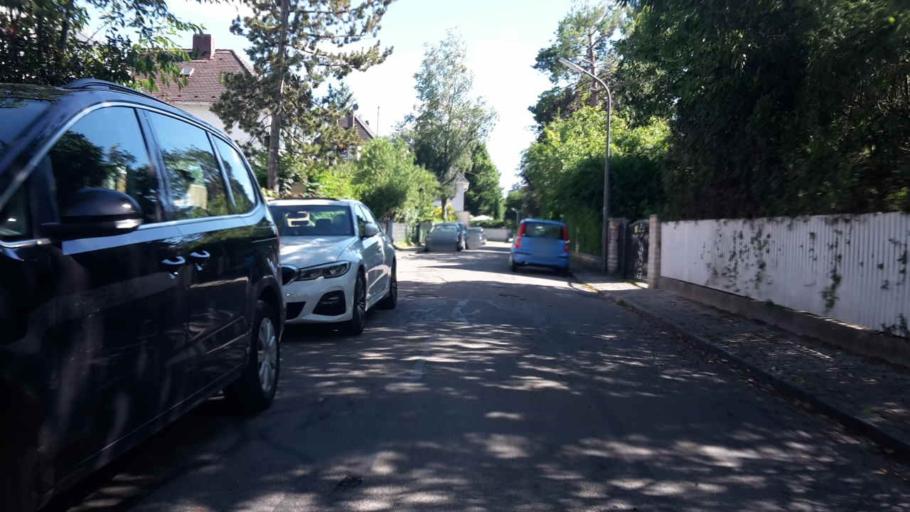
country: DE
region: Bavaria
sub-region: Upper Bavaria
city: Pasing
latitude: 48.1704
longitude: 11.4723
